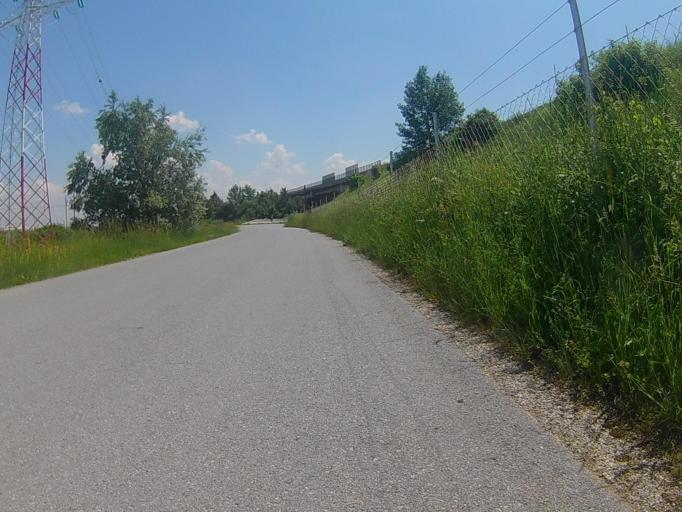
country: SI
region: Hoce-Slivnica
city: Radizel
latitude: 46.4798
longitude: 15.6621
